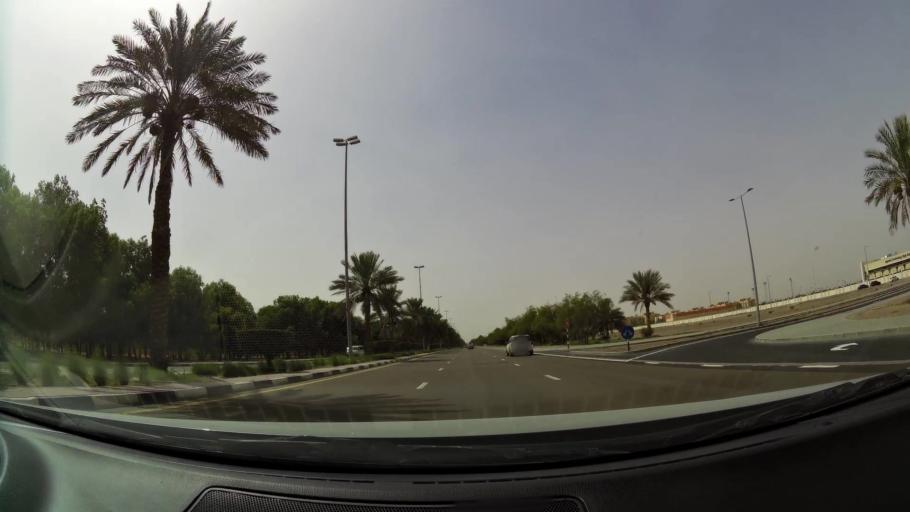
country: AE
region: Abu Dhabi
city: Al Ain
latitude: 24.1782
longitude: 55.6629
